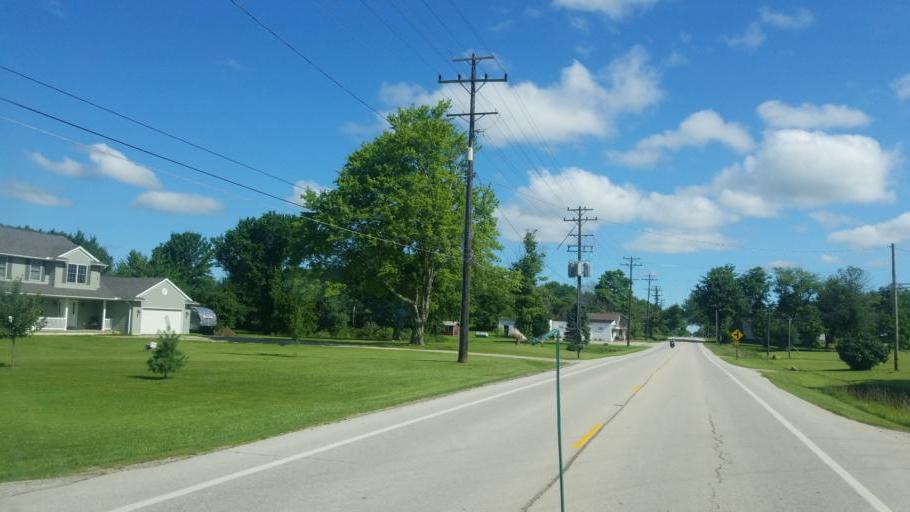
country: US
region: Ohio
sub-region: Ashtabula County
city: Conneaut
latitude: 41.8416
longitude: -80.5724
